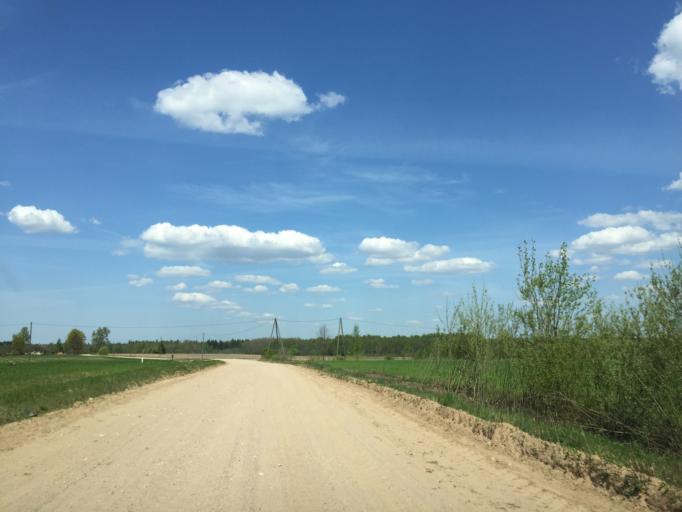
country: LV
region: Limbazu Rajons
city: Limbazi
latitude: 57.3502
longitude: 24.6504
